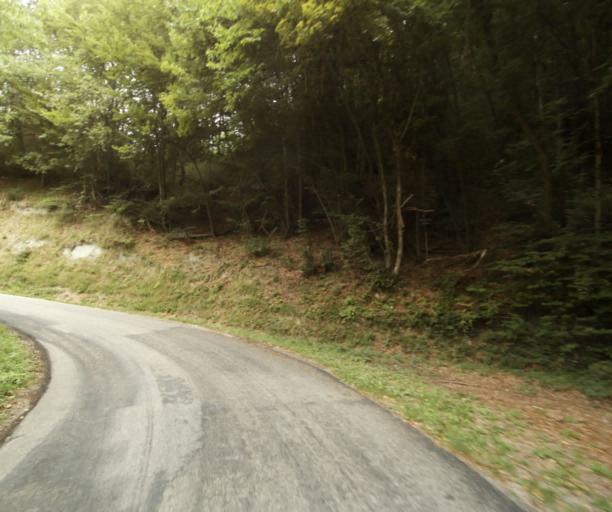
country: FR
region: Rhone-Alpes
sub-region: Departement de l'Isere
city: Saint-Egreve
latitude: 45.2677
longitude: 5.7093
